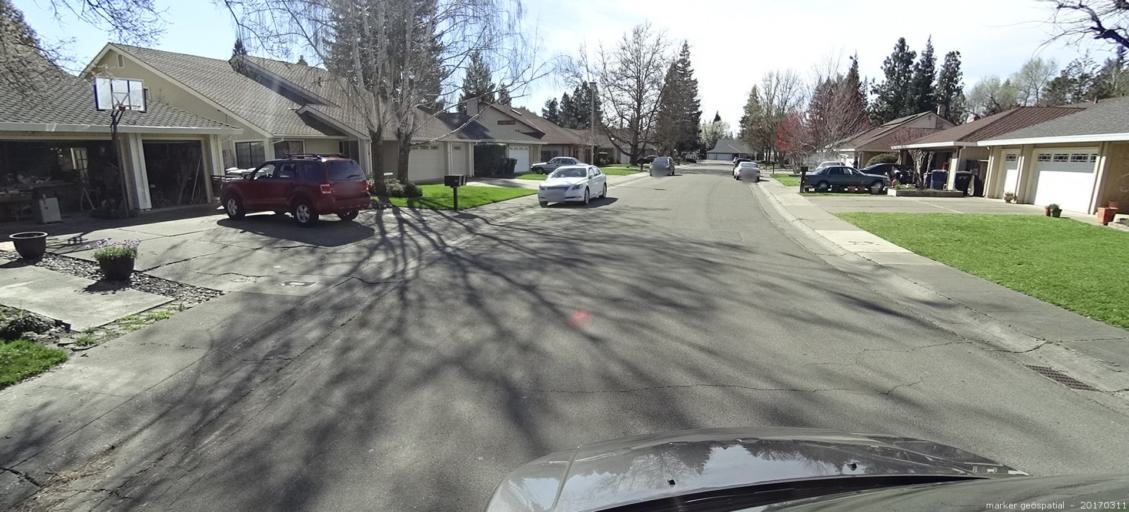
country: US
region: California
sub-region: Yolo County
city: West Sacramento
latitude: 38.4968
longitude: -121.5458
